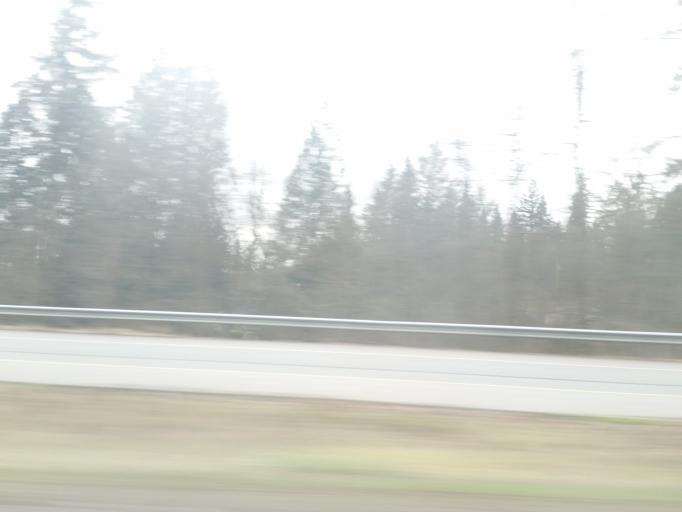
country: US
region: Washington
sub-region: Snohomish County
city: Maltby
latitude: 47.8123
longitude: -122.0842
